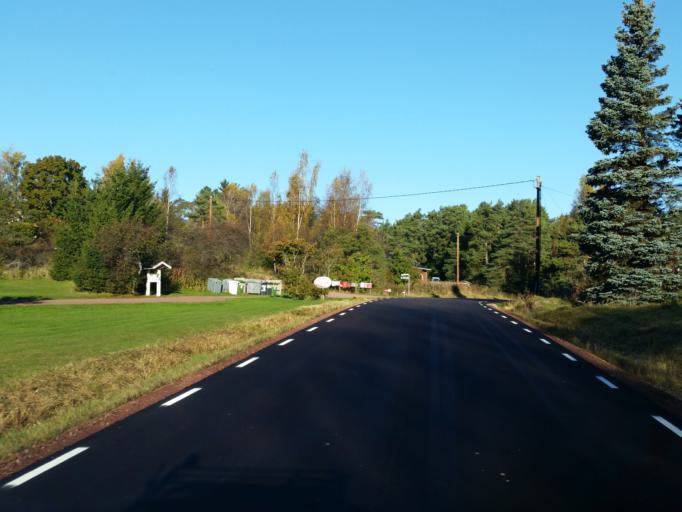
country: AX
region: Alands landsbygd
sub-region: Sund
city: Sund
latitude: 60.2272
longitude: 20.0912
